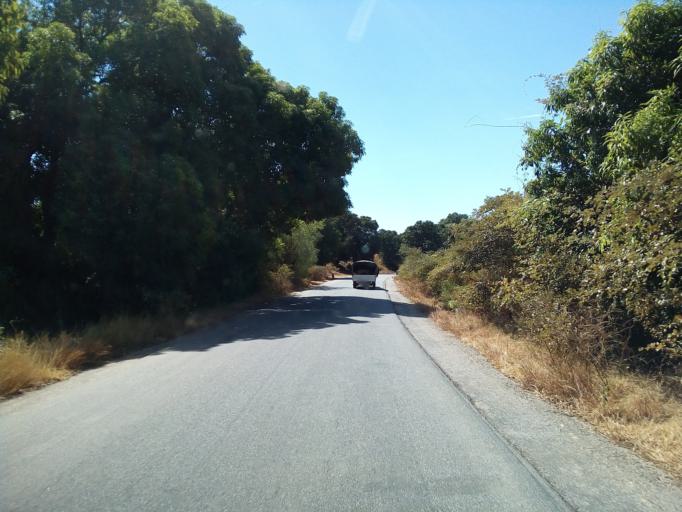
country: MG
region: Betsiboka
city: Maevatanana
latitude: -16.9156
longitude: 46.8692
